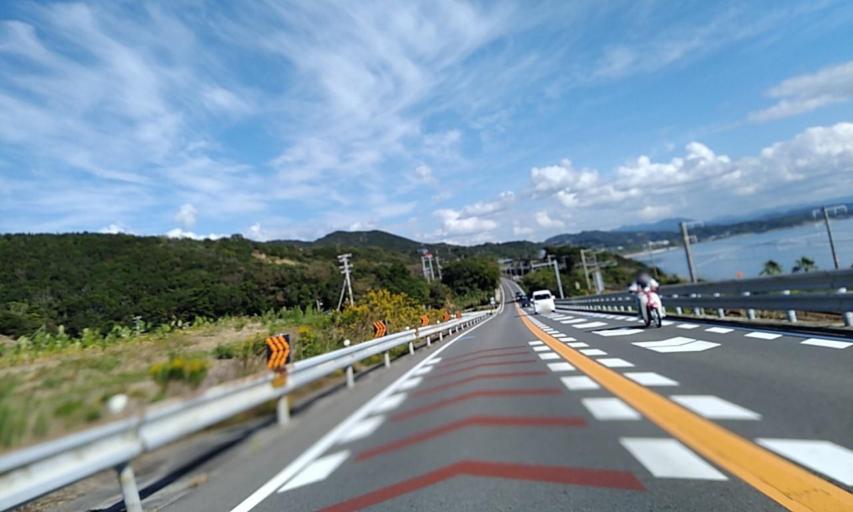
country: JP
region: Wakayama
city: Tanabe
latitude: 33.7822
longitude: 135.2471
